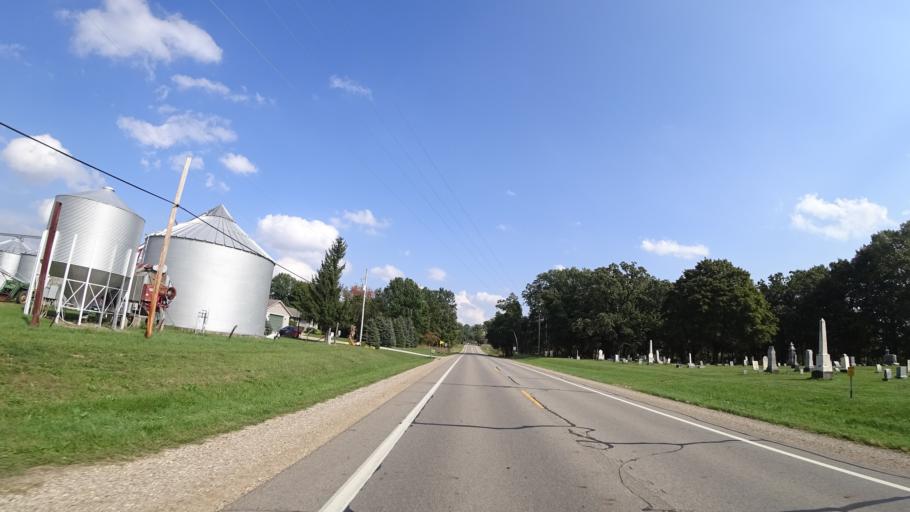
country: US
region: Michigan
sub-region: Saint Joseph County
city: Centreville
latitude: 42.0063
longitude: -85.4776
